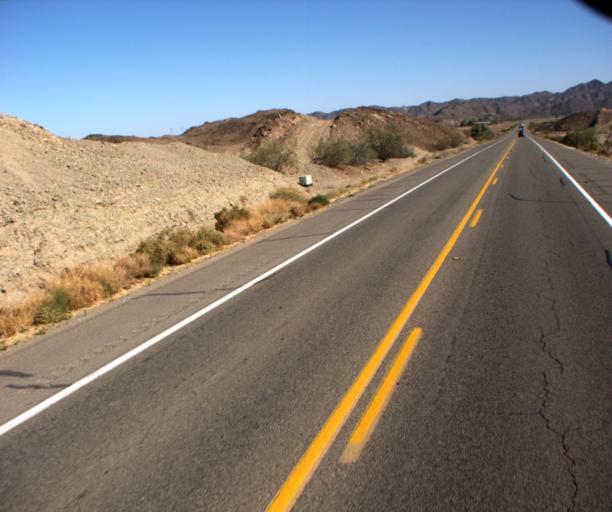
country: US
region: Arizona
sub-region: Yuma County
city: Fortuna Foothills
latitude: 32.7432
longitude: -114.4247
